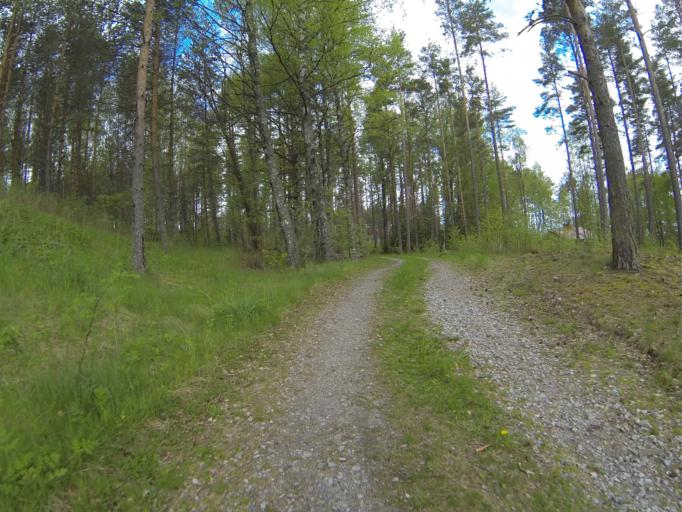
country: FI
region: Varsinais-Suomi
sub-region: Salo
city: Salo
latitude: 60.3484
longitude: 23.1038
